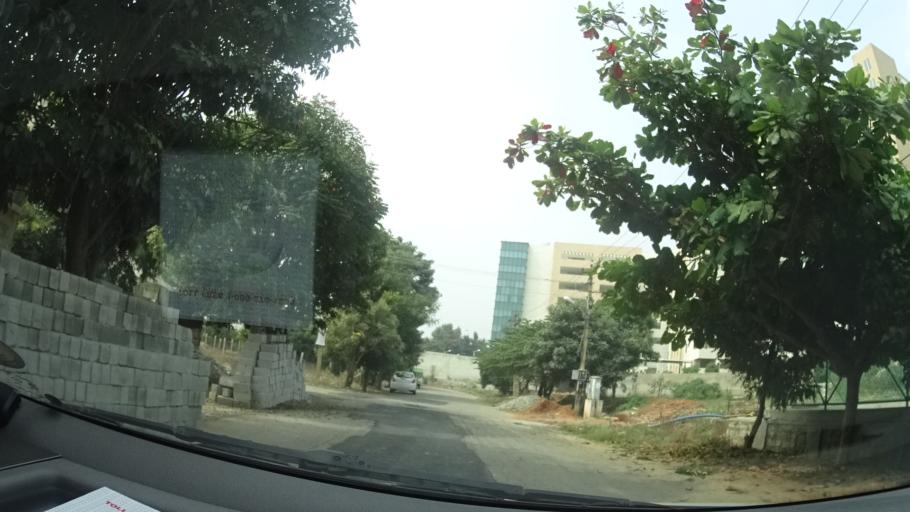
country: IN
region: Karnataka
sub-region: Bangalore Urban
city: Yelahanka
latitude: 13.0468
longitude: 77.6239
